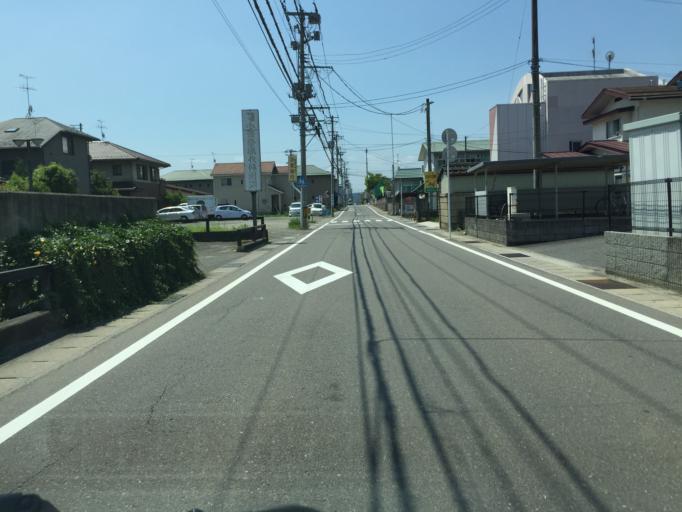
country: JP
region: Fukushima
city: Fukushima-shi
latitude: 37.7485
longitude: 140.4483
